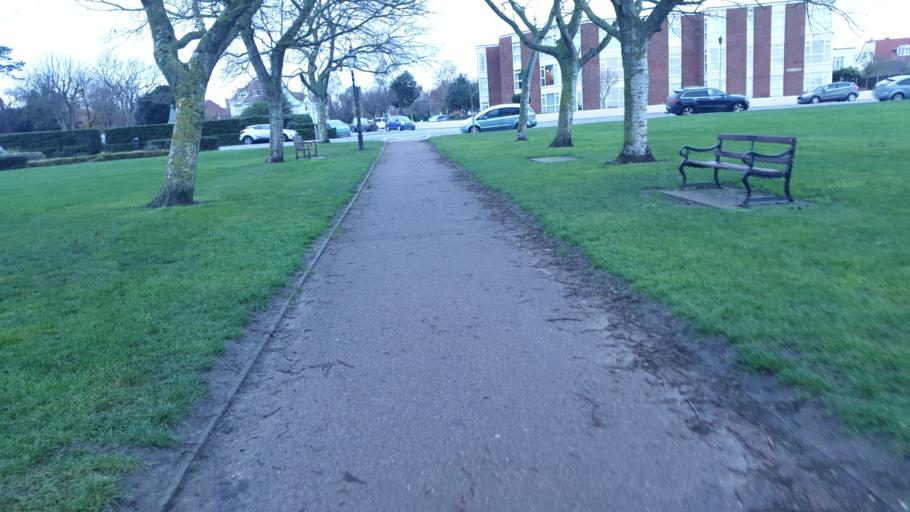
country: GB
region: England
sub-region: Essex
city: Frinton-on-Sea
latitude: 51.8291
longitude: 1.2473
